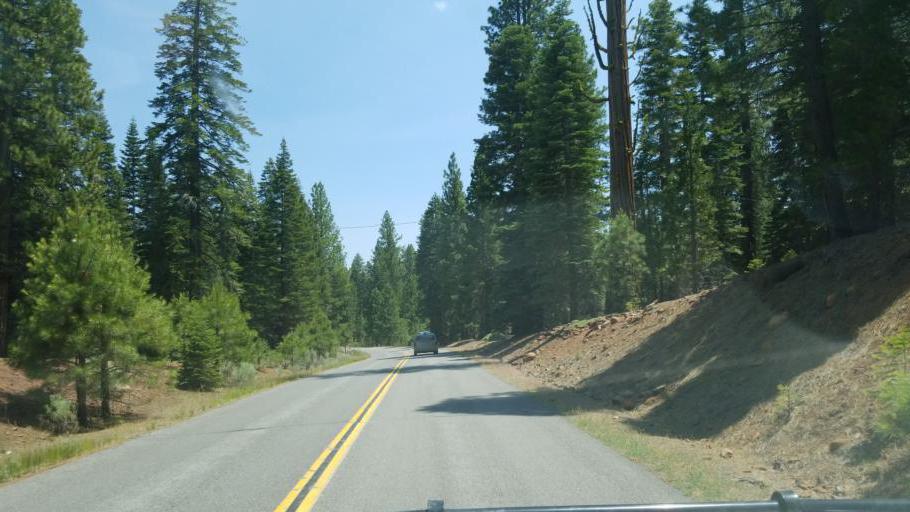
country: US
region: California
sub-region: Lassen County
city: Susanville
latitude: 40.5500
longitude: -120.8165
